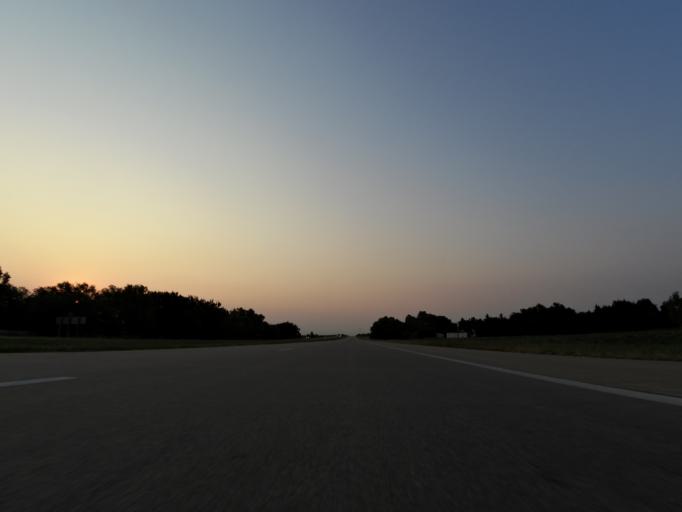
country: US
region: Kansas
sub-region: Reno County
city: Haven
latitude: 37.9286
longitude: -97.8476
